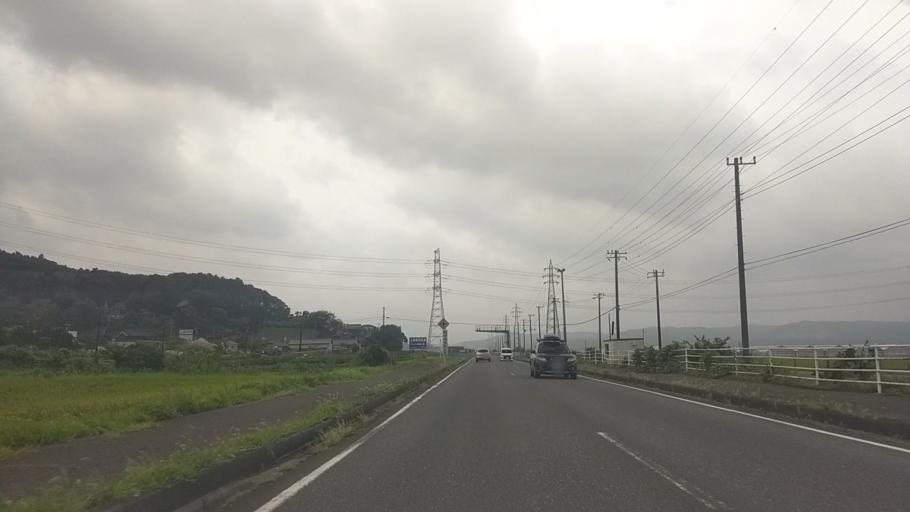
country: JP
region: Chiba
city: Kisarazu
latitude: 35.3467
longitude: 140.0548
